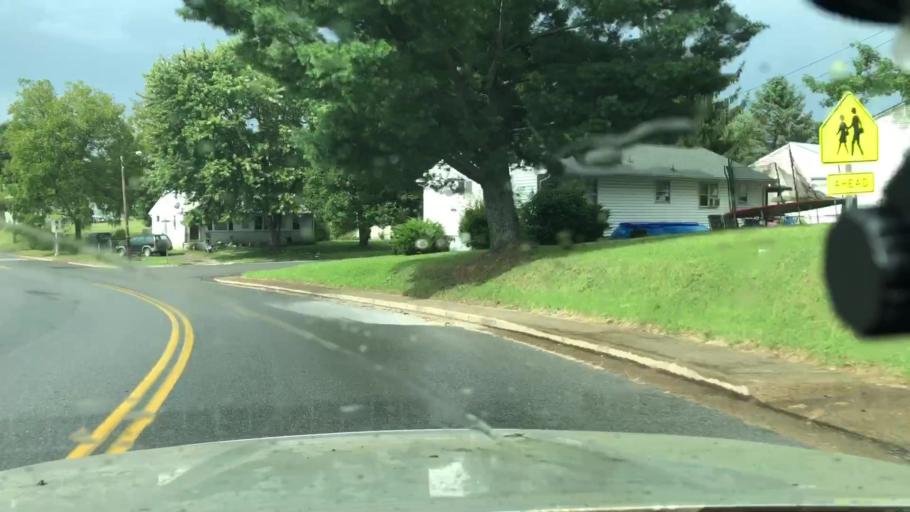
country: US
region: Virginia
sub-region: City of Waynesboro
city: Waynesboro
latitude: 38.0781
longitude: -78.8950
